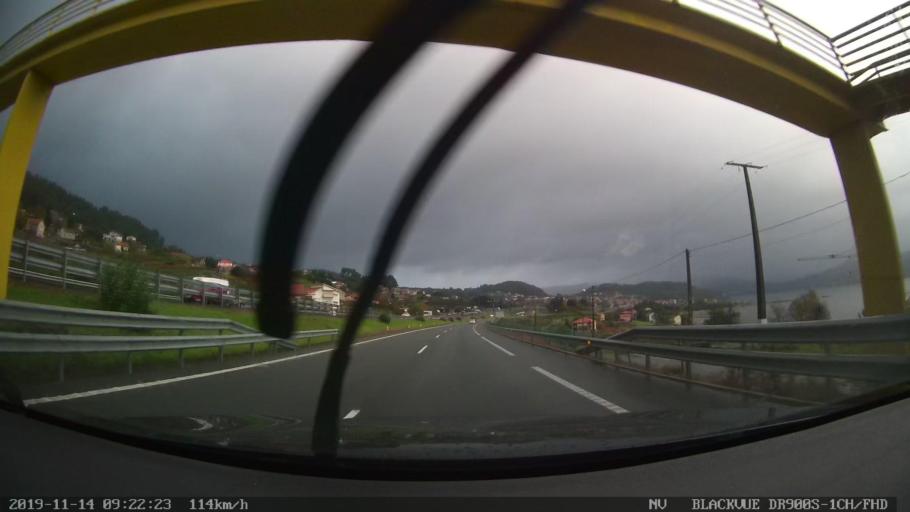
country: ES
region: Galicia
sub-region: Provincia de Pontevedra
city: Redondela
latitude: 42.3123
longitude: -8.6661
